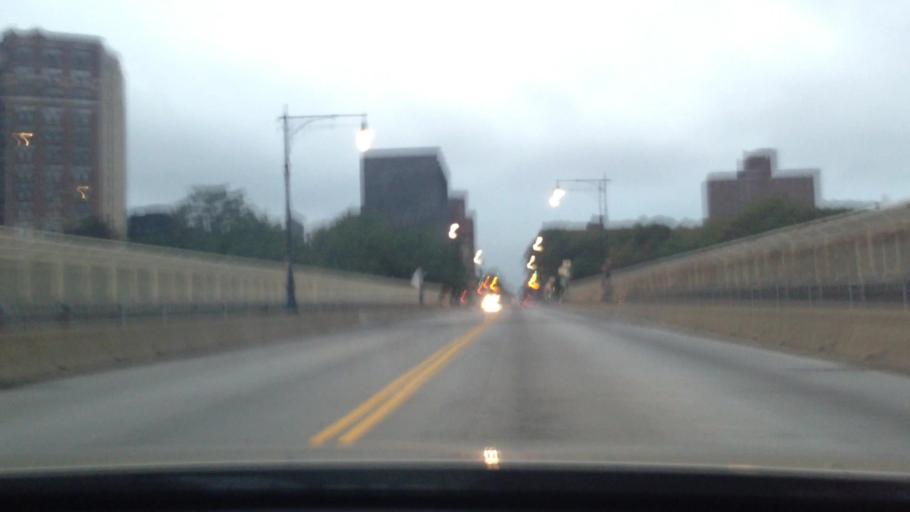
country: US
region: New Jersey
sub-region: Bergen County
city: Edgewater
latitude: 40.8294
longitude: -73.9378
